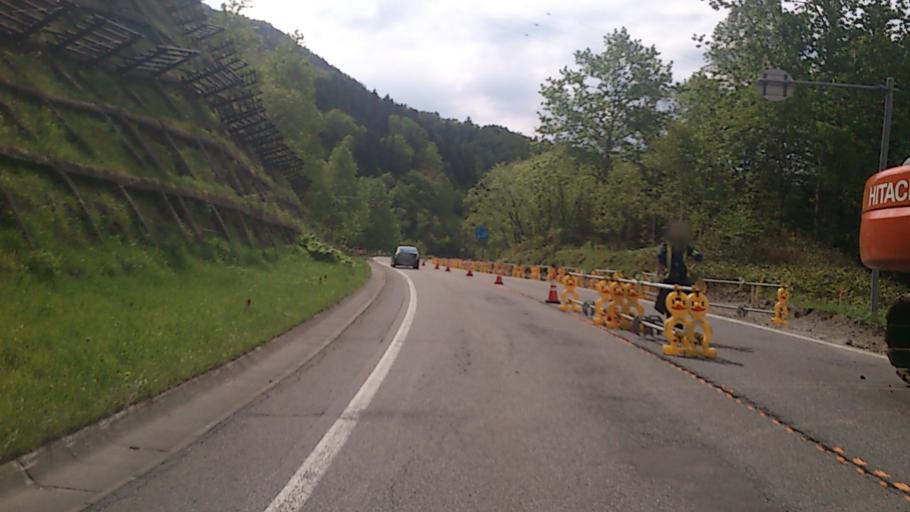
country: JP
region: Hokkaido
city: Kamikawa
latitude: 43.6835
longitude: 143.0335
